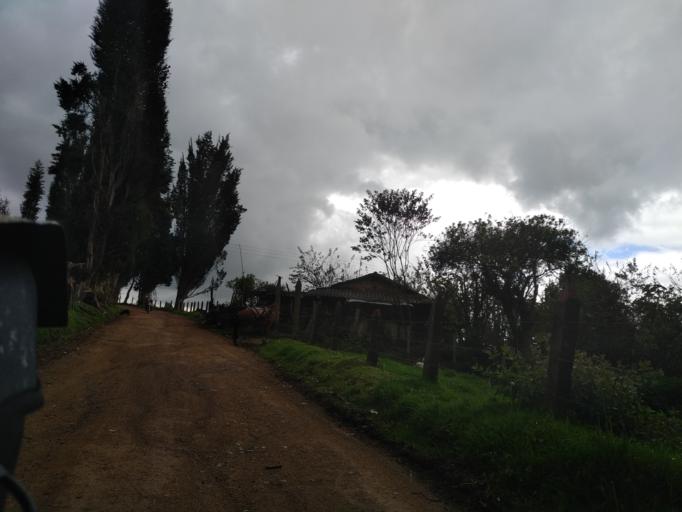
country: CO
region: Boyaca
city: Sotaquira
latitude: 5.7657
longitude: -73.2690
